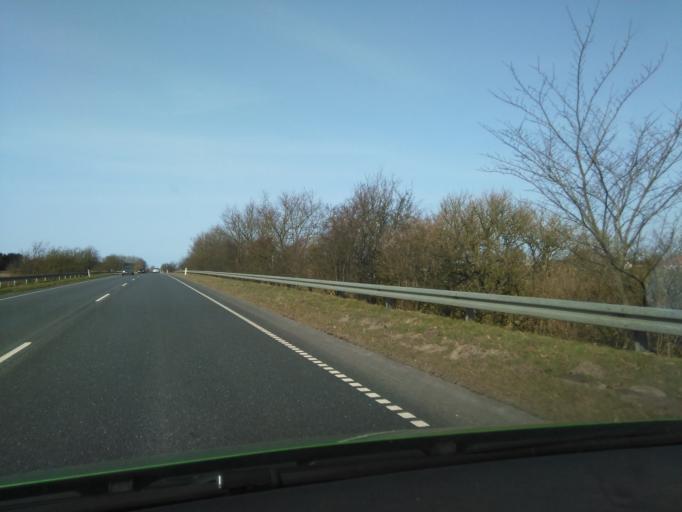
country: DK
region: Central Jutland
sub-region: Silkeborg Kommune
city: Kjellerup
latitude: 56.2604
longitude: 9.4372
